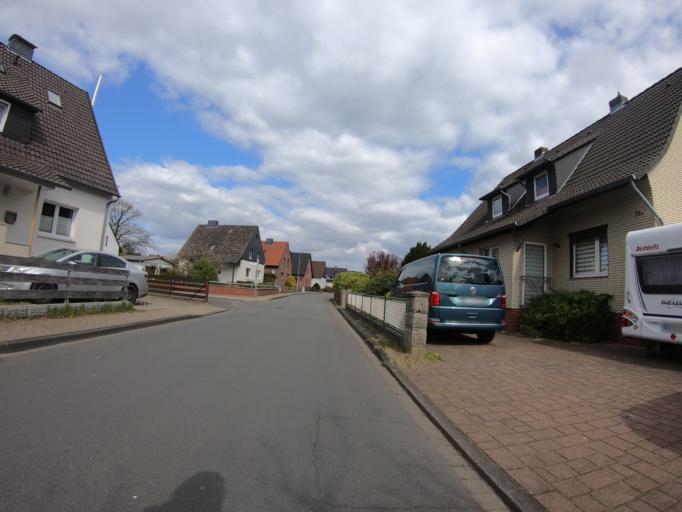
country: DE
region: Lower Saxony
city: Gifhorn
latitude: 52.4834
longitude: 10.5217
